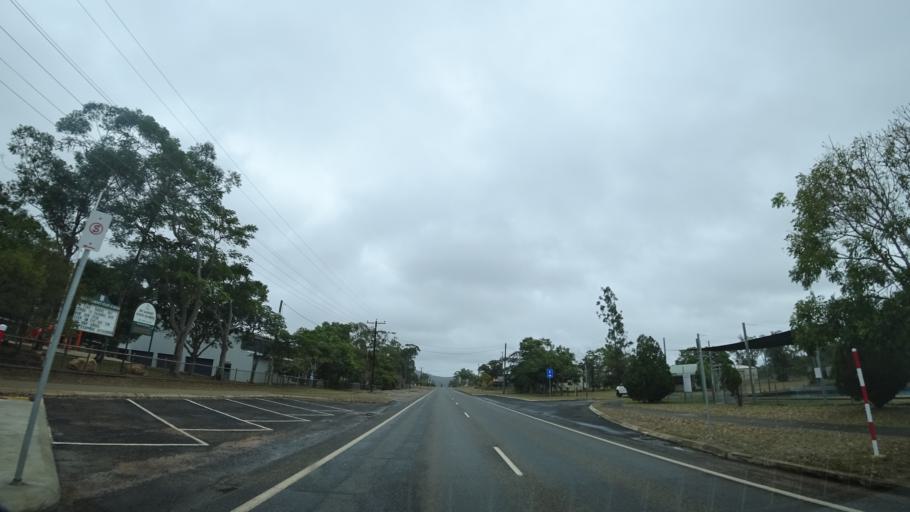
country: AU
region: Queensland
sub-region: Tablelands
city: Ravenshoe
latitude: -17.6801
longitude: 145.1217
